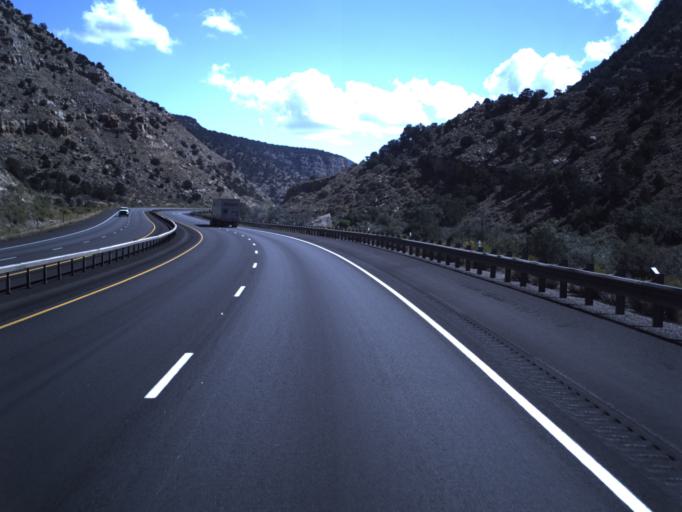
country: US
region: Utah
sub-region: Sevier County
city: Salina
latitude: 38.9039
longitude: -111.6866
